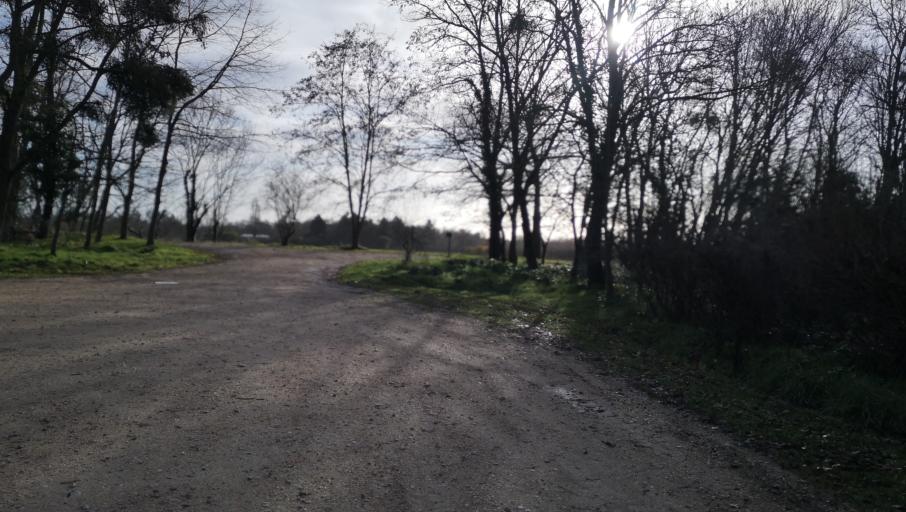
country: FR
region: Centre
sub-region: Departement du Loiret
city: Saint-Hilaire-Saint-Mesmin
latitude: 47.8749
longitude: 1.8301
